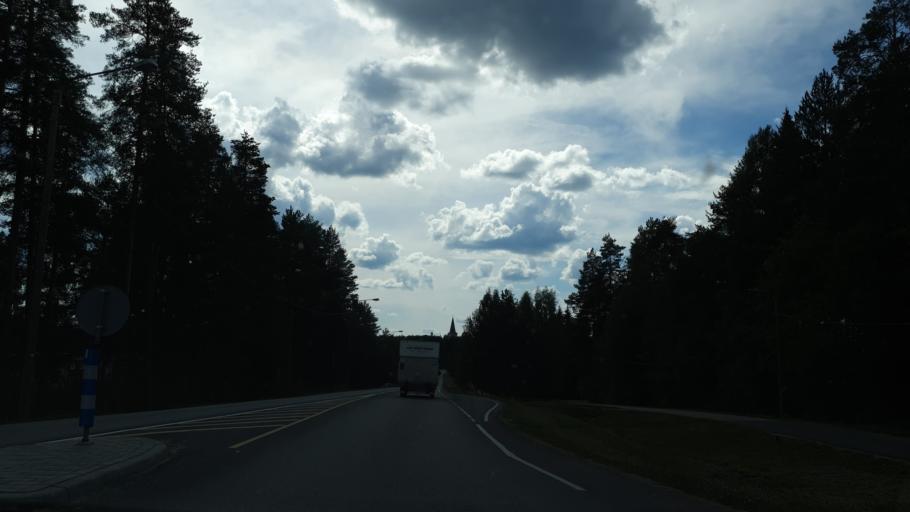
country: FI
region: Kainuu
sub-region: Kajaani
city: Sotkamo
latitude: 64.1378
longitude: 28.4124
